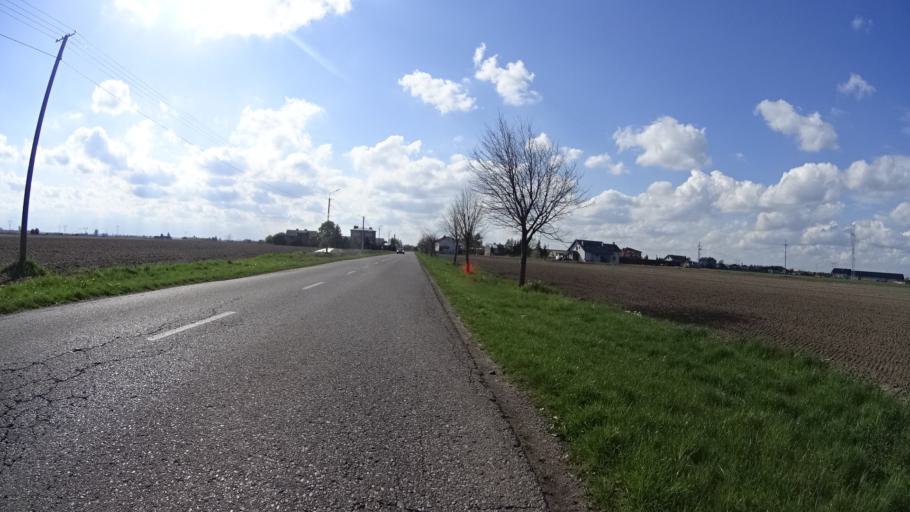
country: PL
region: Masovian Voivodeship
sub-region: Powiat warszawski zachodni
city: Jozefow
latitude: 52.2337
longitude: 20.6797
